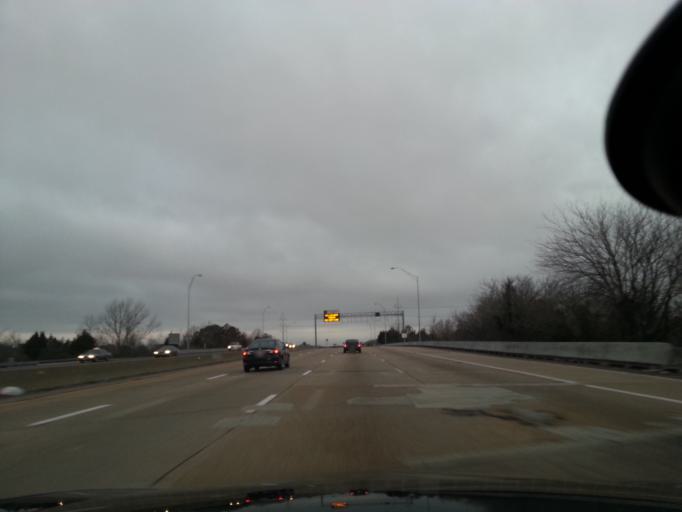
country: US
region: Virginia
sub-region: City of Chesapeake
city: Chesapeake
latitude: 36.8387
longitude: -76.1593
